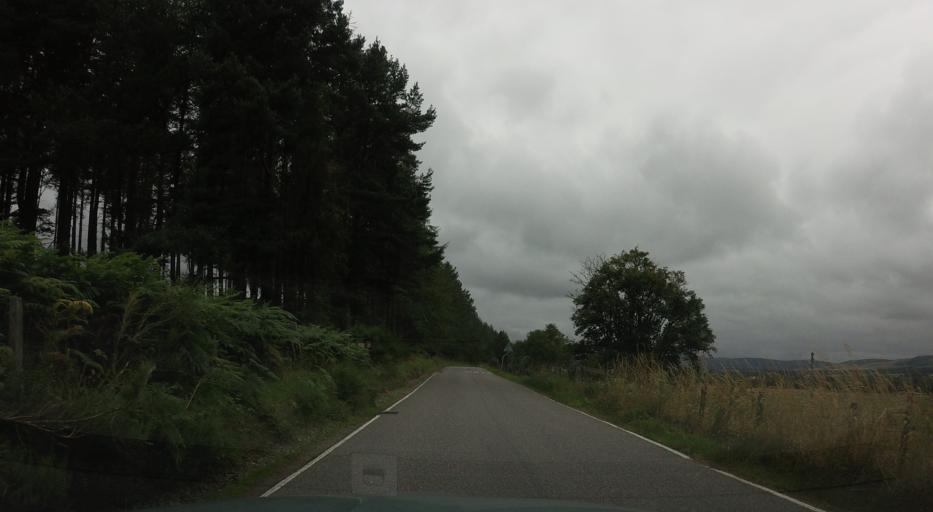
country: GB
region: Scotland
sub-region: Aberdeenshire
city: Banchory
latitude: 57.0151
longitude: -2.5396
